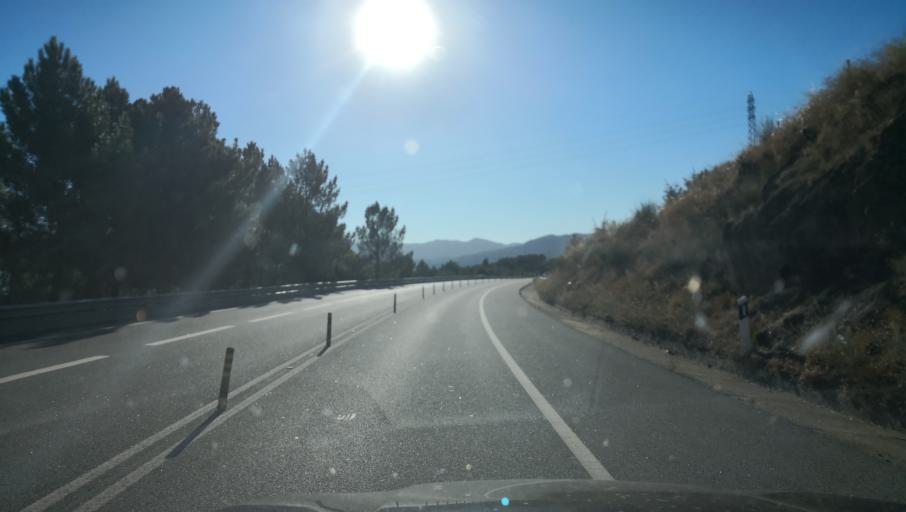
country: PT
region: Vila Real
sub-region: Vila Real
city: Vila Real
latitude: 41.3254
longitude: -7.6926
